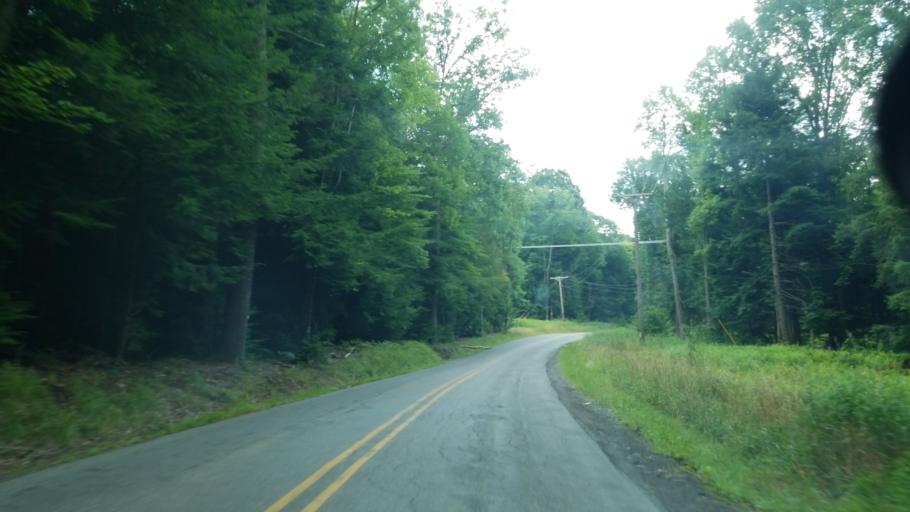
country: US
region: Pennsylvania
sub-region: Jefferson County
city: Brookville
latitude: 41.2304
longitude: -79.0583
